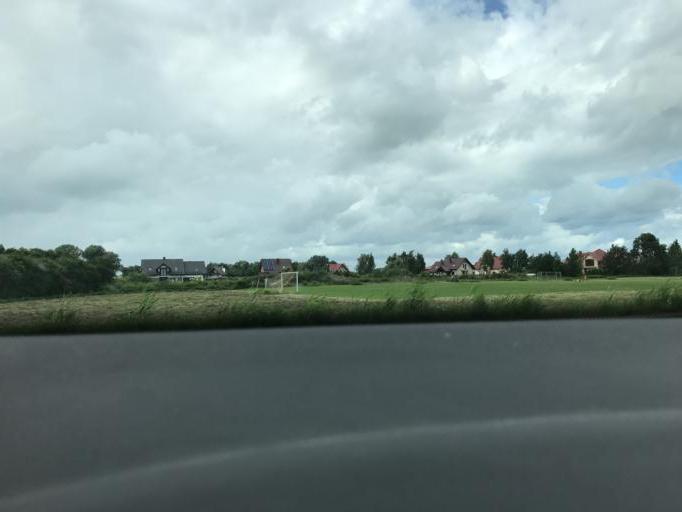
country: PL
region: Pomeranian Voivodeship
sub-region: Powiat gdanski
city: Pruszcz Gdanski
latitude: 54.2717
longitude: 18.6816
